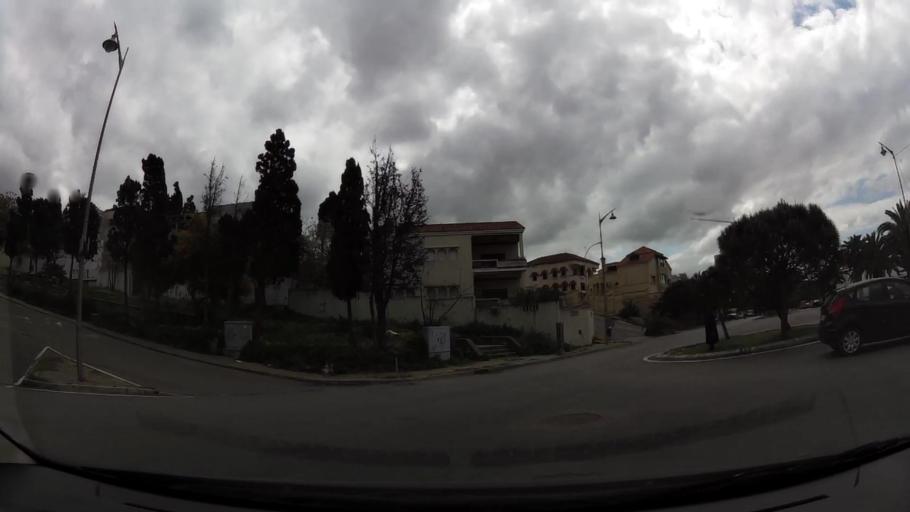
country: MA
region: Tanger-Tetouan
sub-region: Tanger-Assilah
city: Tangier
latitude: 35.7757
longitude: -5.7759
